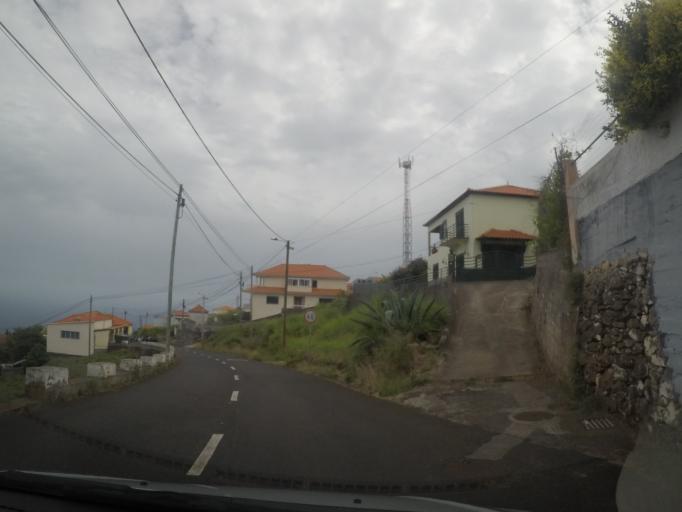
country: PT
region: Madeira
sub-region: Santa Cruz
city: Santa Cruz
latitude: 32.6847
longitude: -16.8102
